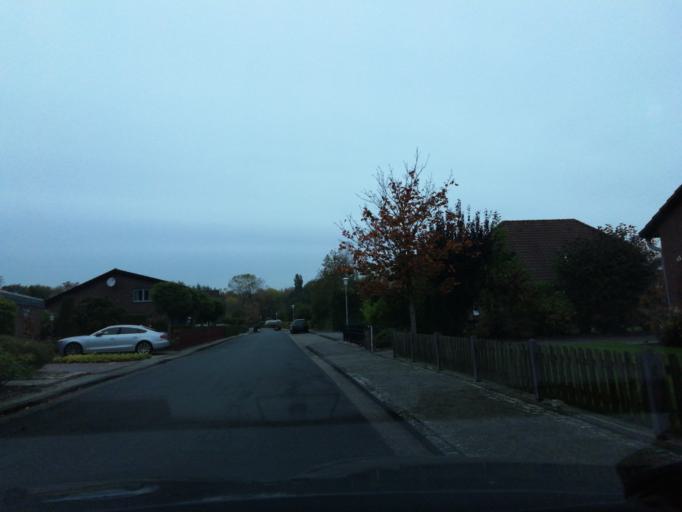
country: DE
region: Lower Saxony
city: Fedderwarden
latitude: 53.6321
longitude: 8.0299
